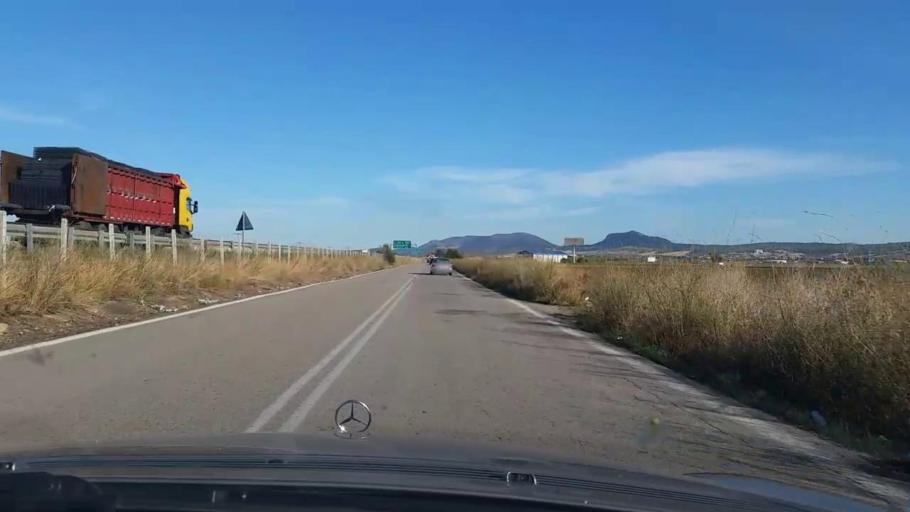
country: GR
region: Central Greece
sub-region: Nomos Voiotias
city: Thivai
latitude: 38.3669
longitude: 23.3030
